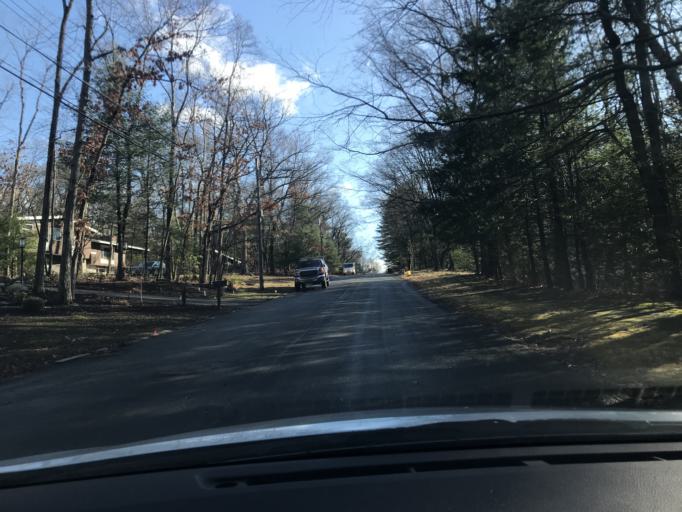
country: US
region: Massachusetts
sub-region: Middlesex County
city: Lexington
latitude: 42.4792
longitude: -71.2293
